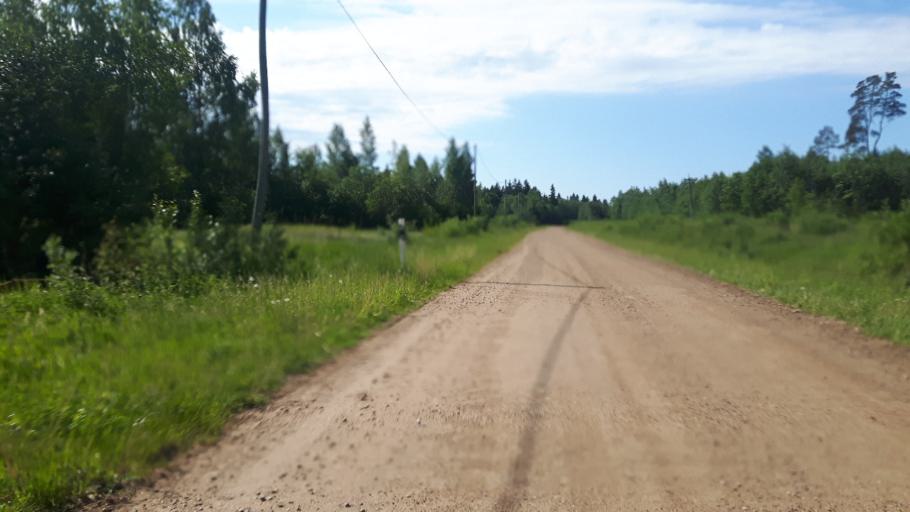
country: EE
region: Paernumaa
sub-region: Vaendra vald (alev)
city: Vandra
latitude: 58.6713
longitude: 25.0288
